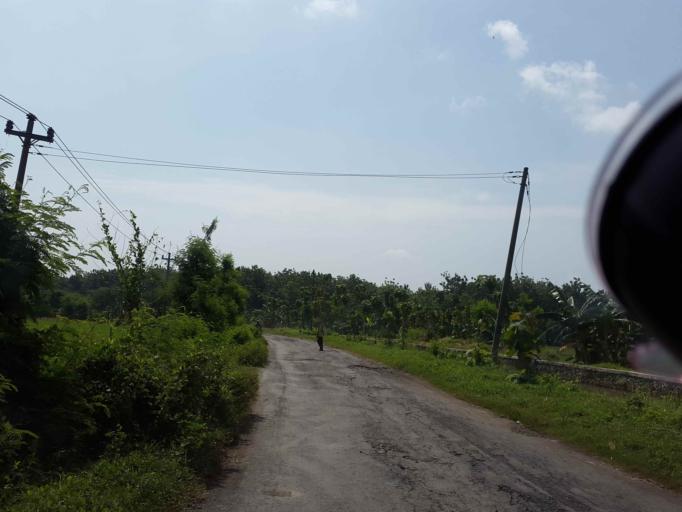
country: ID
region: Central Java
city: Pemalang
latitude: -6.9515
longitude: 109.3597
